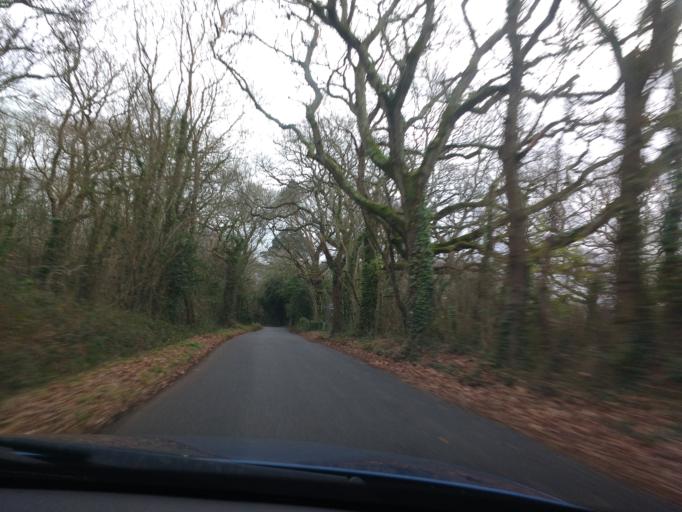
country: GB
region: England
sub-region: Isle of Wight
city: Shalfleet
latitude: 50.7120
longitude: -1.3925
